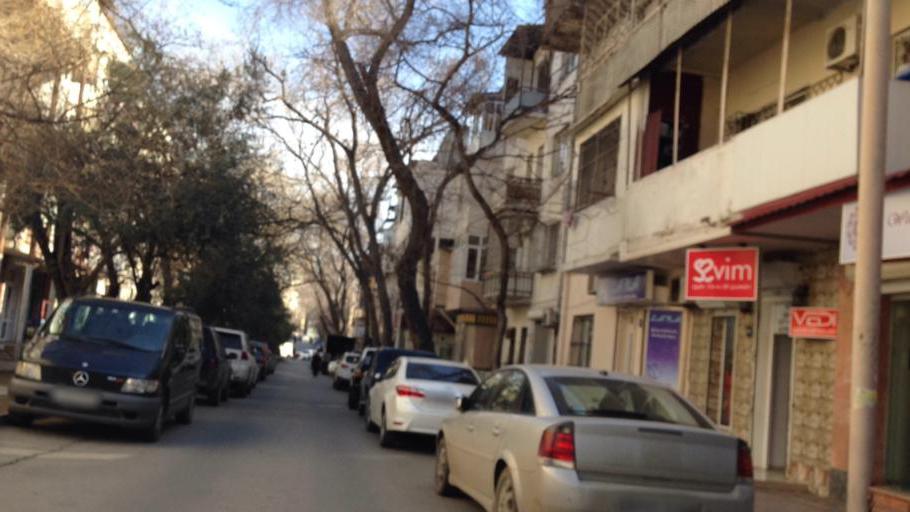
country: AZ
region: Baki
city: Baku
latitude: 40.3887
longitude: 49.8433
